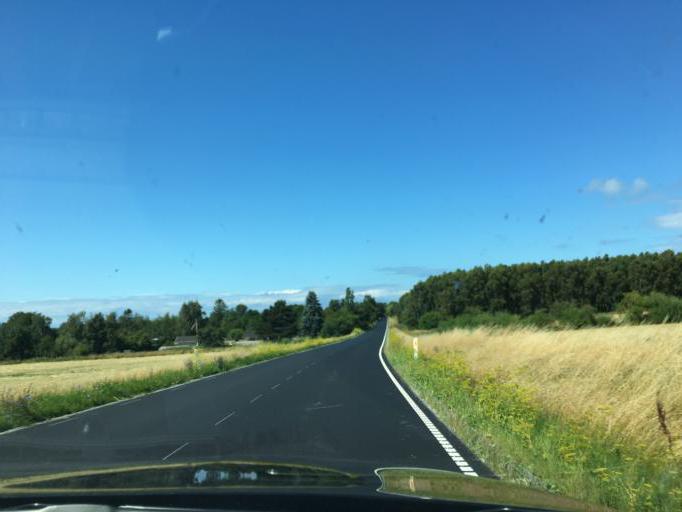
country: DK
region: Capital Region
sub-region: Gribskov Kommune
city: Helsinge
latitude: 56.0852
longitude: 12.1779
